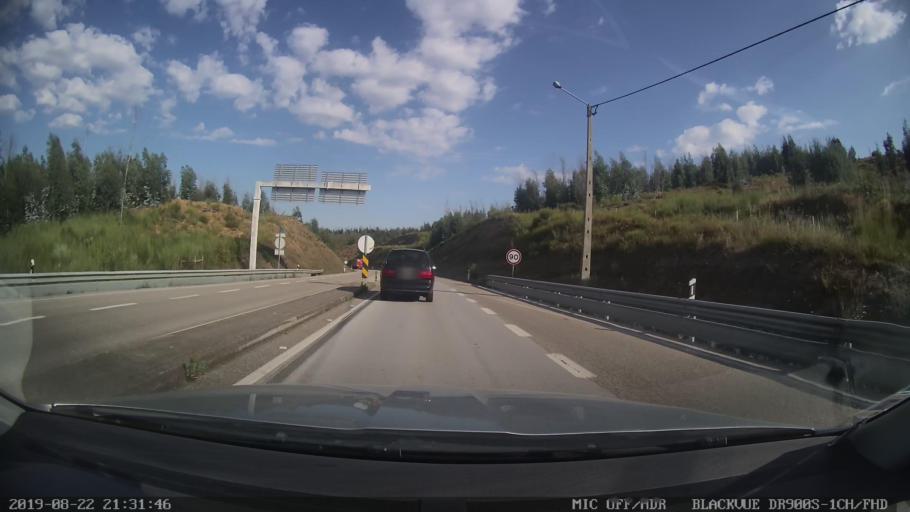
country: PT
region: Leiria
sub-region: Pedrogao Grande
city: Pedrogao Grande
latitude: 39.9235
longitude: -8.1565
